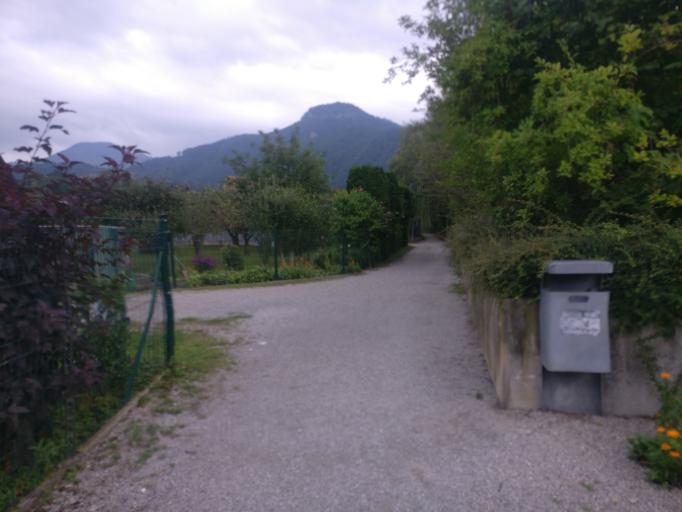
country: AT
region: Styria
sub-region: Politischer Bezirk Graz-Umgebung
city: Frohnleiten
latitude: 47.2666
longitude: 15.3216
